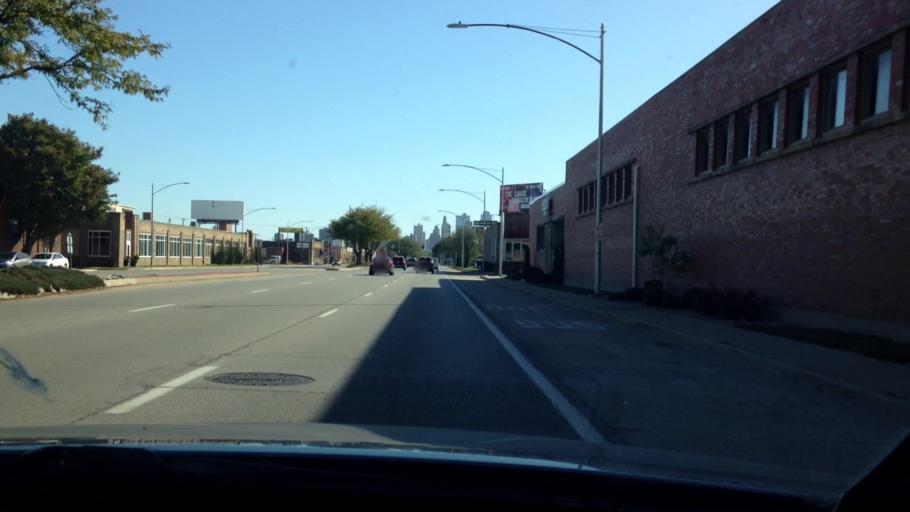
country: US
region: Missouri
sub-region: Clay County
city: North Kansas City
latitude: 39.1369
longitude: -94.5807
